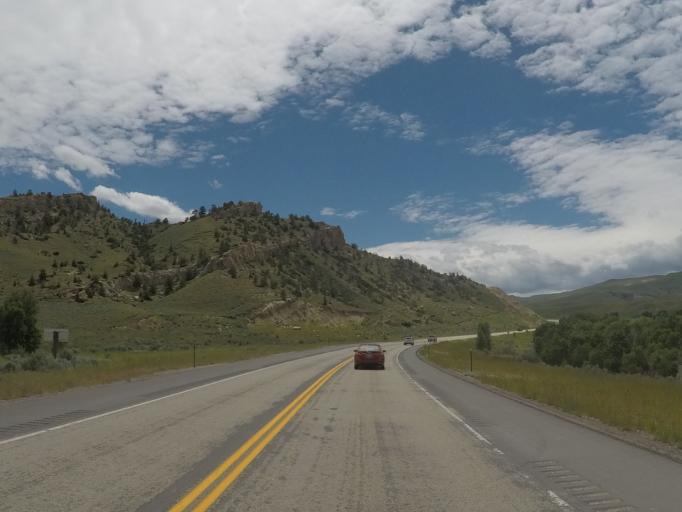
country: US
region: Wyoming
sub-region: Park County
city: Cody
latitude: 44.7311
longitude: -109.2165
